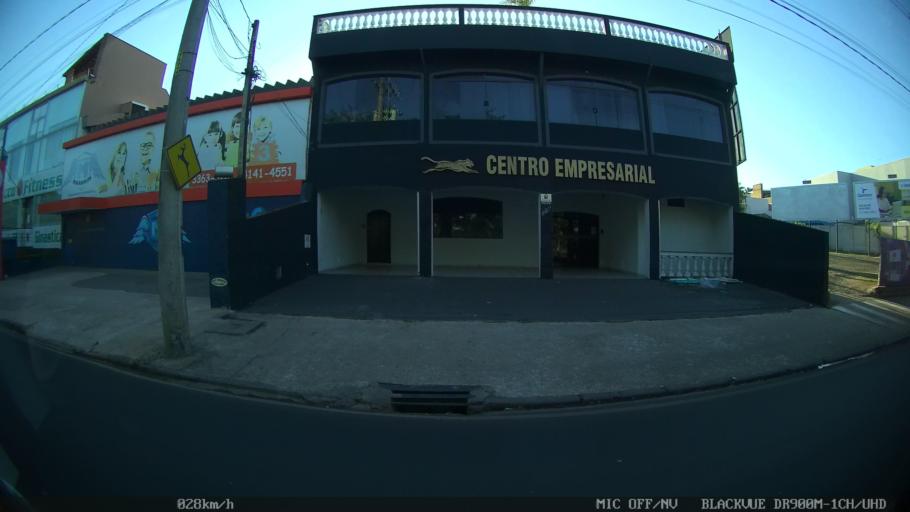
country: BR
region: Sao Paulo
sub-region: Sao Jose Do Rio Preto
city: Sao Jose do Rio Preto
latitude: -20.8070
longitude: -49.3661
